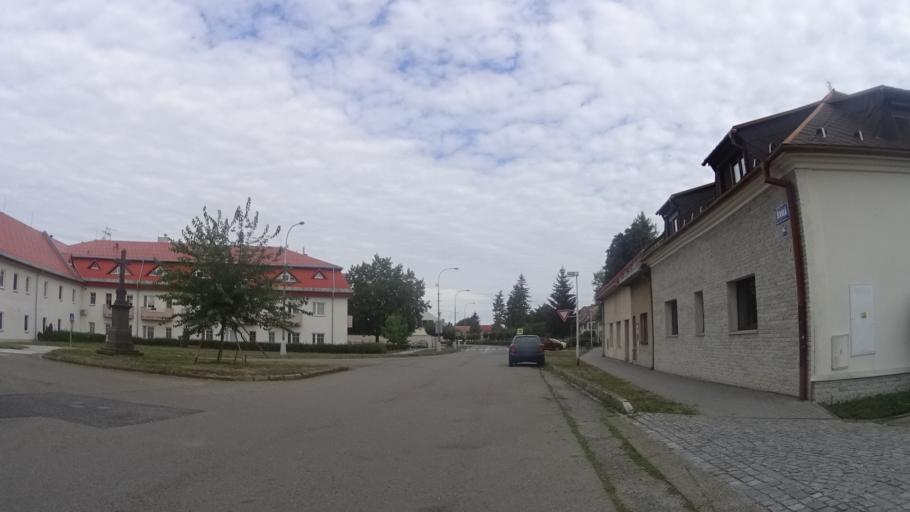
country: CZ
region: Olomoucky
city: Tovacov
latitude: 49.4307
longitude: 17.2887
